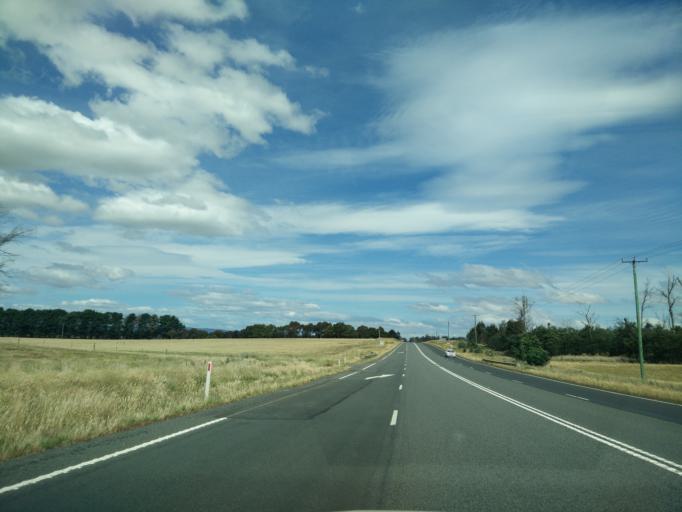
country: AU
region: Tasmania
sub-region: Northern Midlands
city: Evandale
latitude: -41.7163
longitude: 147.3074
